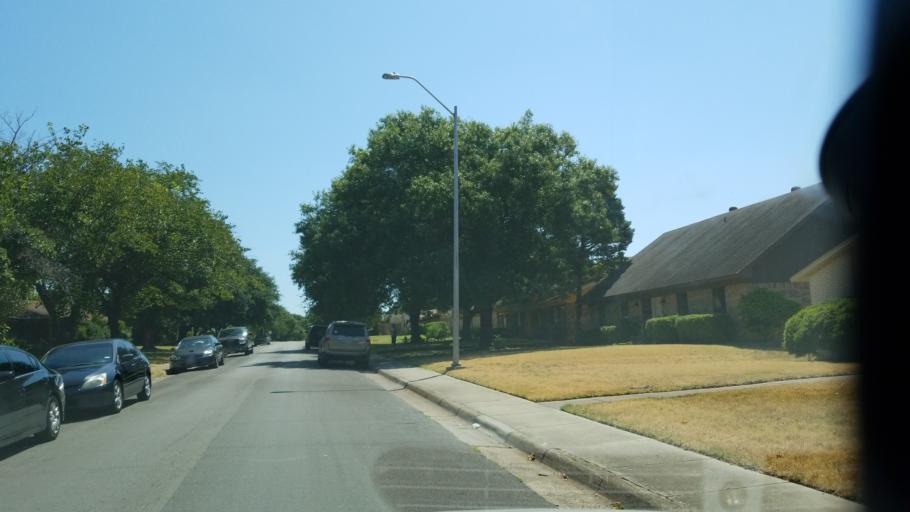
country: US
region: Texas
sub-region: Dallas County
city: Duncanville
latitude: 32.6533
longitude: -96.8972
